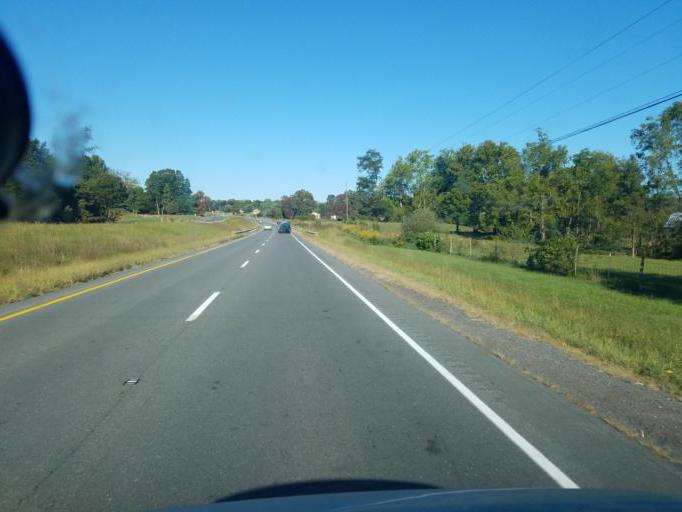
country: US
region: Virginia
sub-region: Culpeper County
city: Merrimac
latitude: 38.4534
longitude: -78.1053
